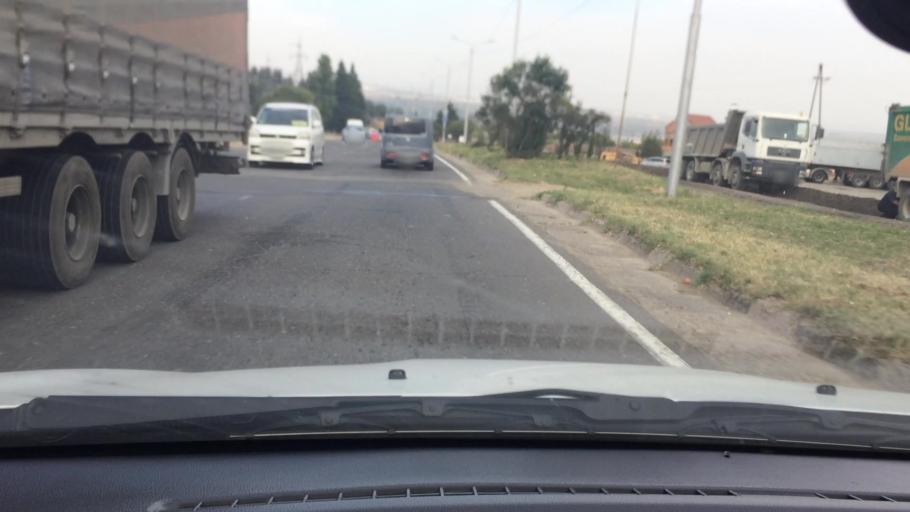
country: GE
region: T'bilisi
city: Tbilisi
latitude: 41.6467
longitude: 44.8983
